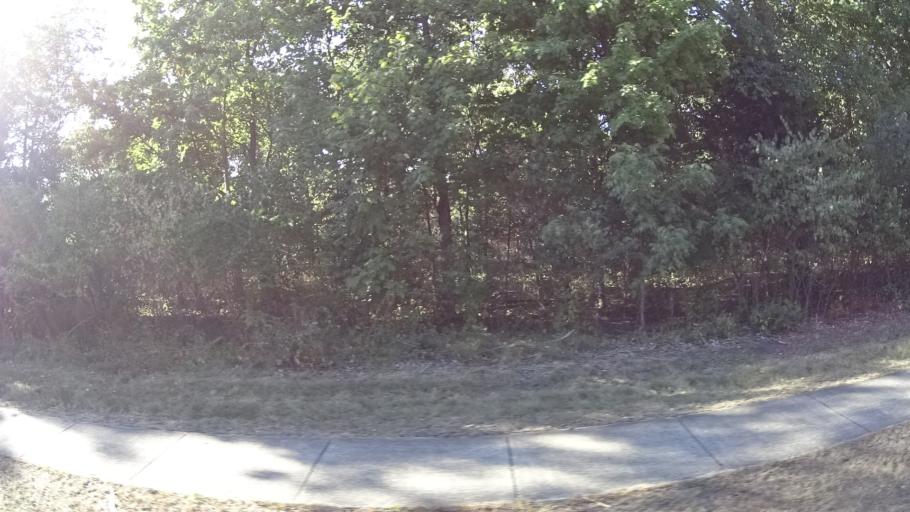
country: US
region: Ohio
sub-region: Erie County
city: Sandusky
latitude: 41.6068
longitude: -82.7049
